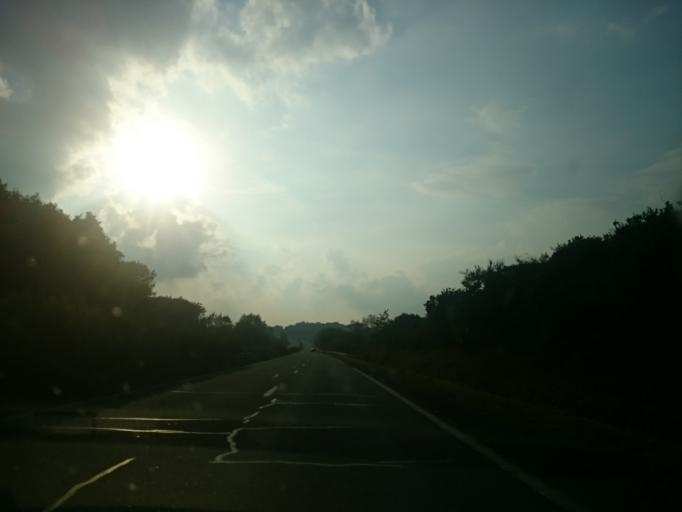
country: FR
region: Brittany
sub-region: Departement du Finistere
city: La Roche-Maurice
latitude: 48.5024
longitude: -4.1663
